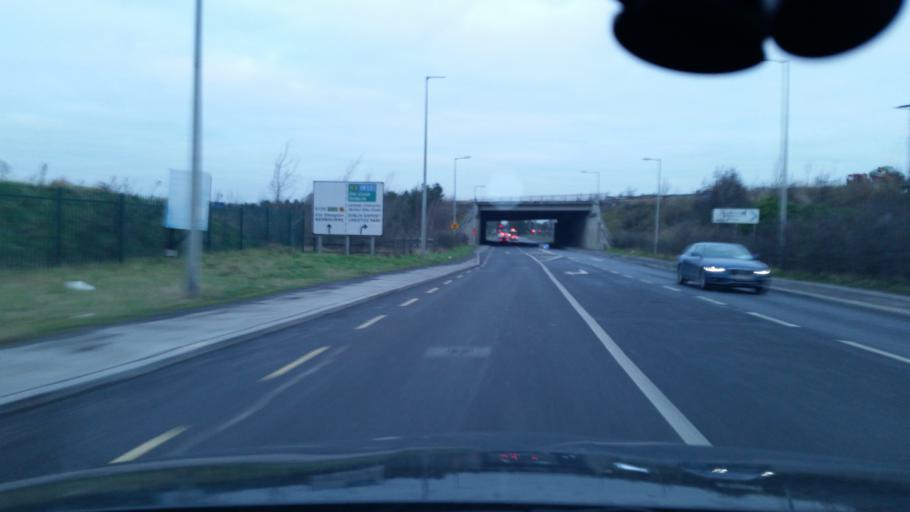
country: IE
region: Leinster
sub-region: Dublin City
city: Finglas
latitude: 53.4184
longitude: -6.3229
